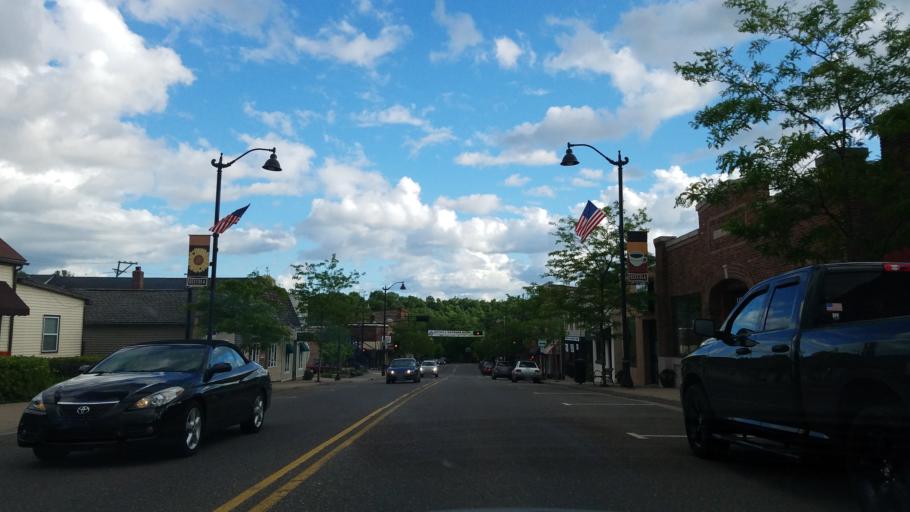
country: US
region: Wisconsin
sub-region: Polk County
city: Osceola
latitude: 45.3217
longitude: -92.7054
